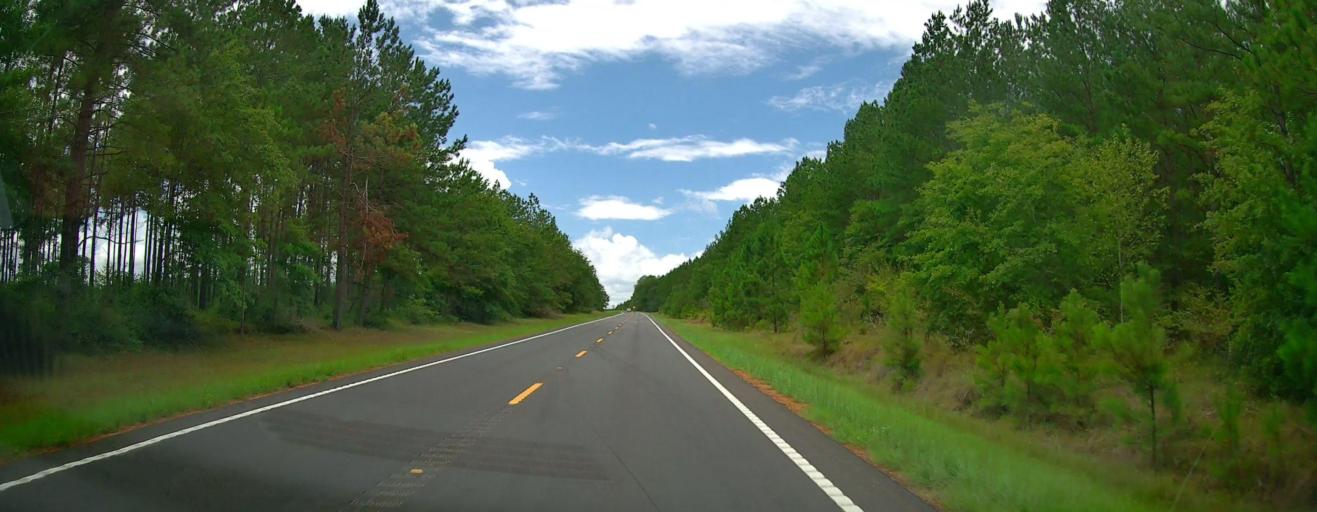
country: US
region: Georgia
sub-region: Dooly County
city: Vienna
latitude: 32.0786
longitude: -83.6139
